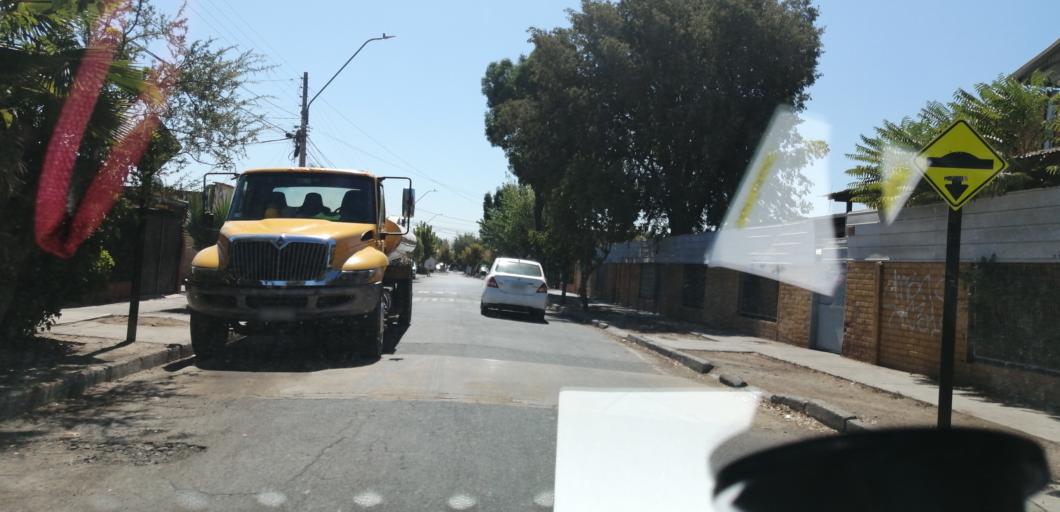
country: CL
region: Santiago Metropolitan
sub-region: Provincia de Santiago
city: Lo Prado
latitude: -33.4320
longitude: -70.7645
